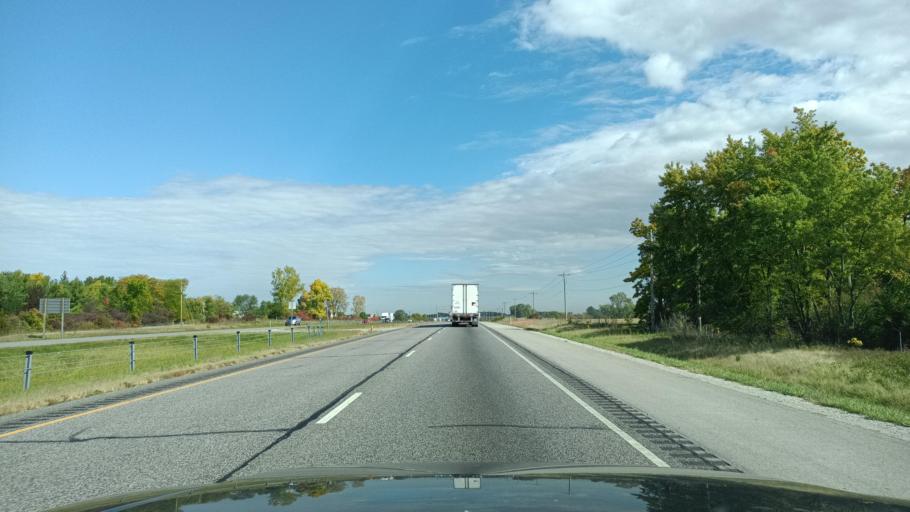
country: US
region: Indiana
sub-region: Huntington County
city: Roanoke
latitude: 40.9478
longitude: -85.3012
